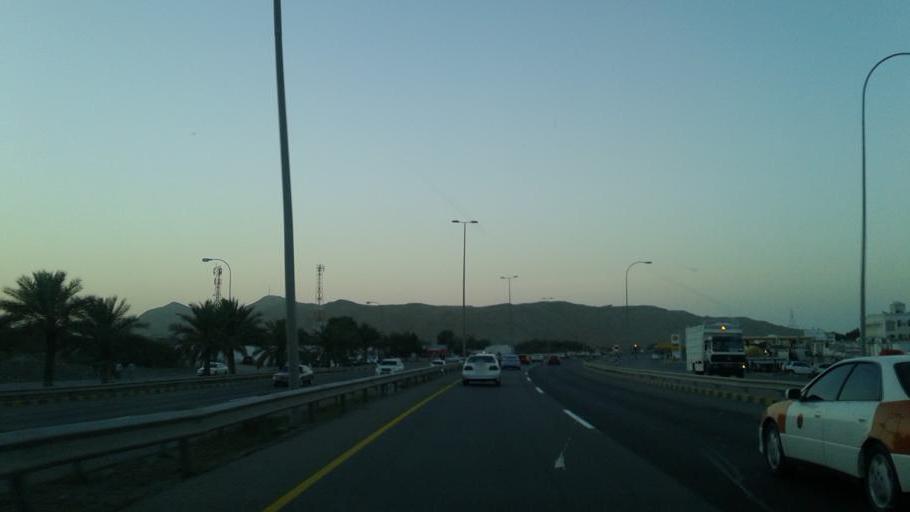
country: OM
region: Muhafazat ad Dakhiliyah
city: Bidbid
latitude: 23.5244
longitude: 58.1893
